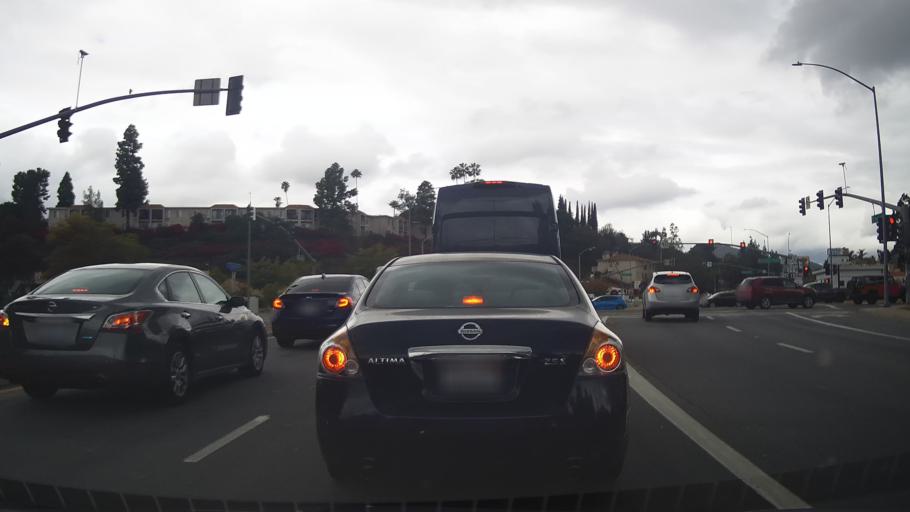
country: US
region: California
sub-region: San Diego County
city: La Mesa
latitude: 32.7772
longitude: -117.0178
